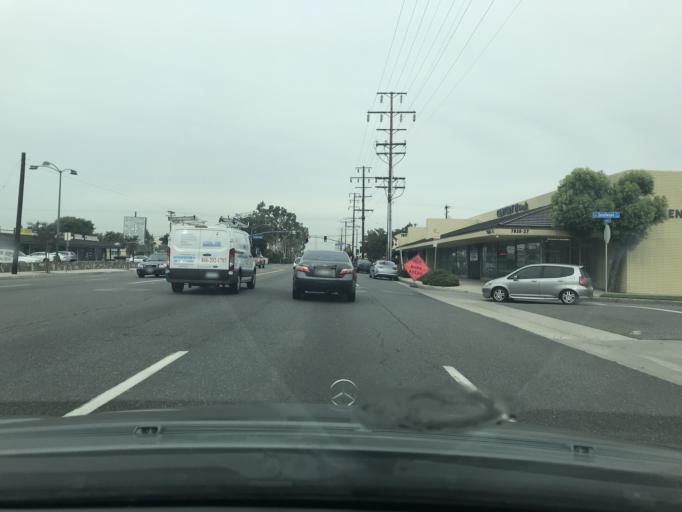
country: US
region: California
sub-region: Los Angeles County
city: Downey
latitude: 33.9552
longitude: -118.1331
